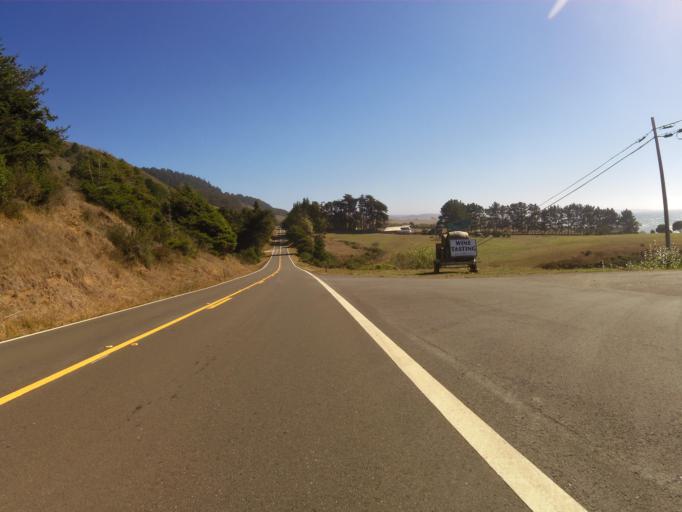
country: US
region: California
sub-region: Mendocino County
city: Fort Bragg
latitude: 39.5929
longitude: -123.7805
